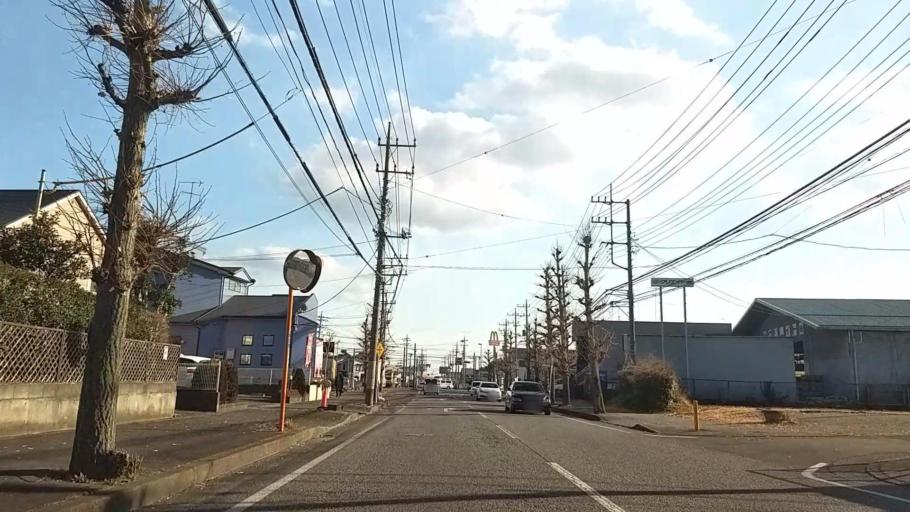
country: JP
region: Kanagawa
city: Atsugi
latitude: 35.4543
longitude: 139.3286
